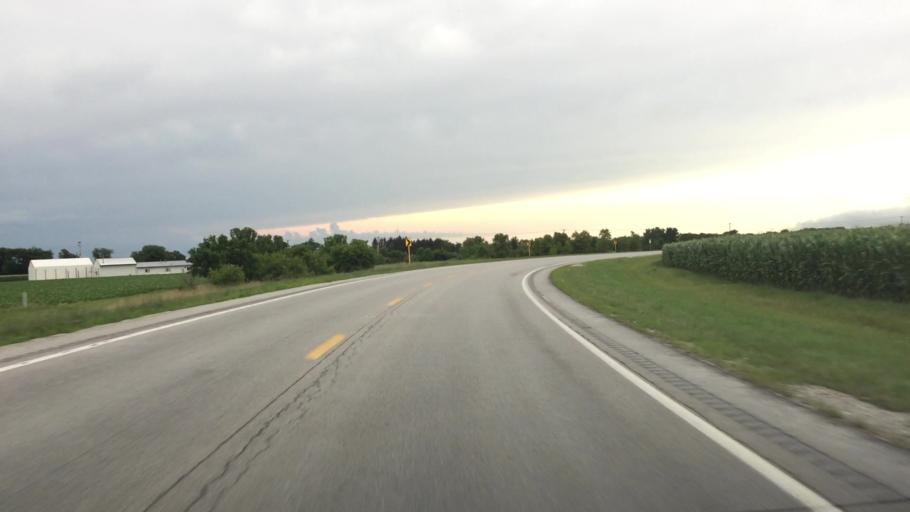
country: US
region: Illinois
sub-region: Hancock County
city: Hamilton
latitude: 40.3661
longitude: -91.3422
